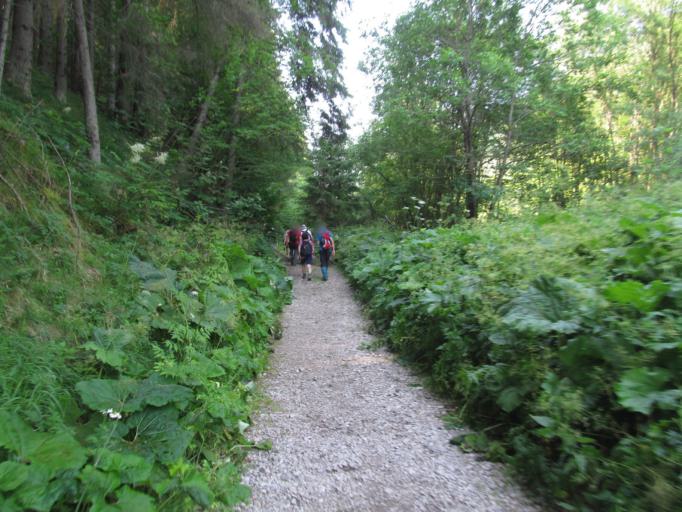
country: SK
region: Kosicky
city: Dobsina
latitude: 48.9404
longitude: 20.3433
